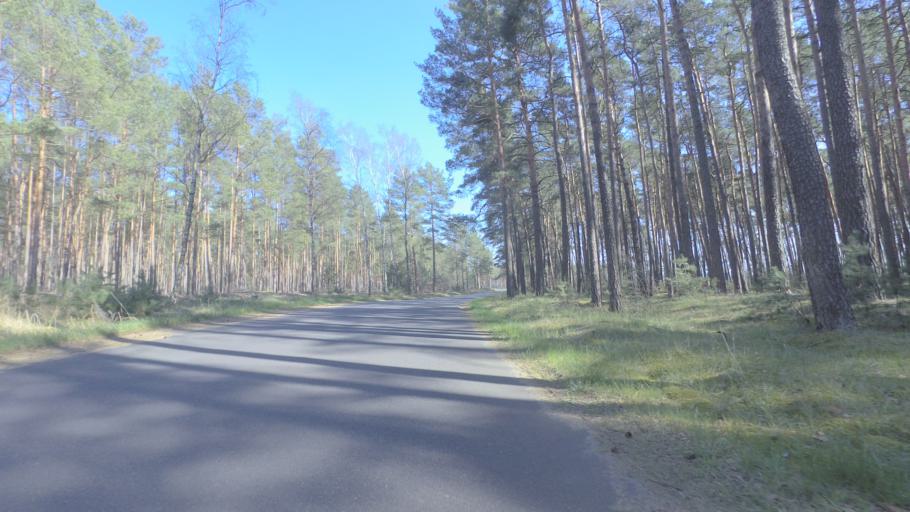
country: DE
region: Brandenburg
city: Munchehofe
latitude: 52.1629
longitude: 13.8076
